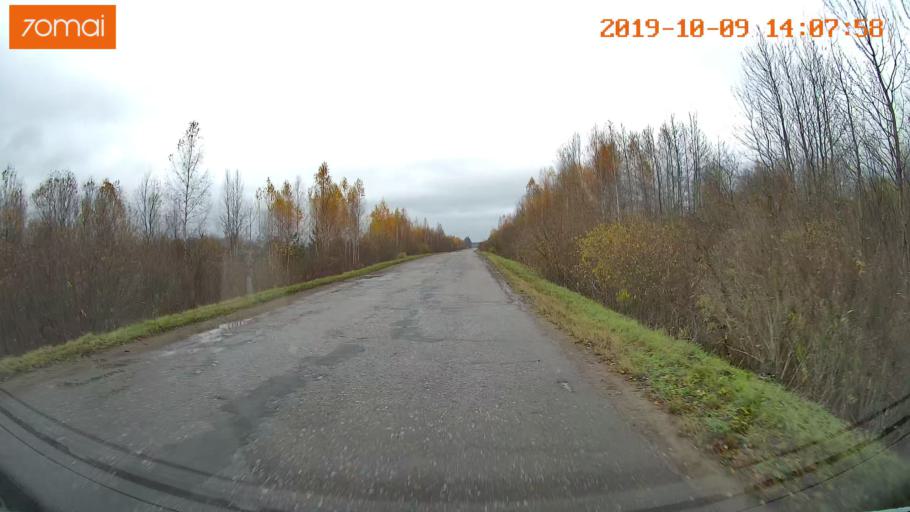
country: RU
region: Kostroma
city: Buy
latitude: 58.4740
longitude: 41.4298
